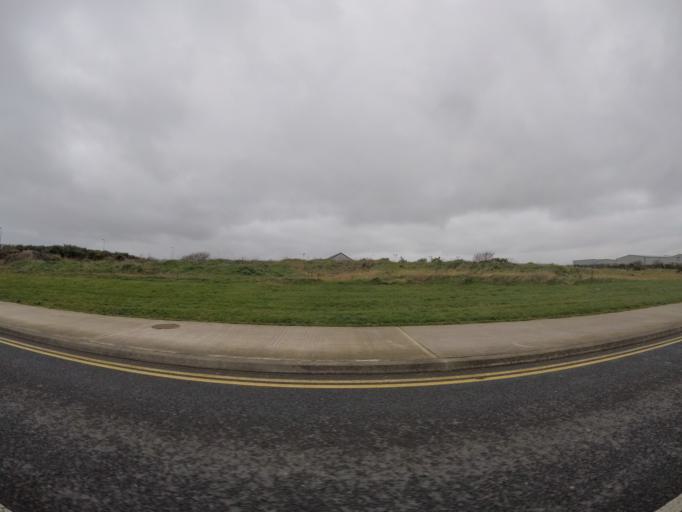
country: IE
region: Munster
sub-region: Waterford
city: Tra Mhor
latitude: 52.1652
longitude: -7.1332
